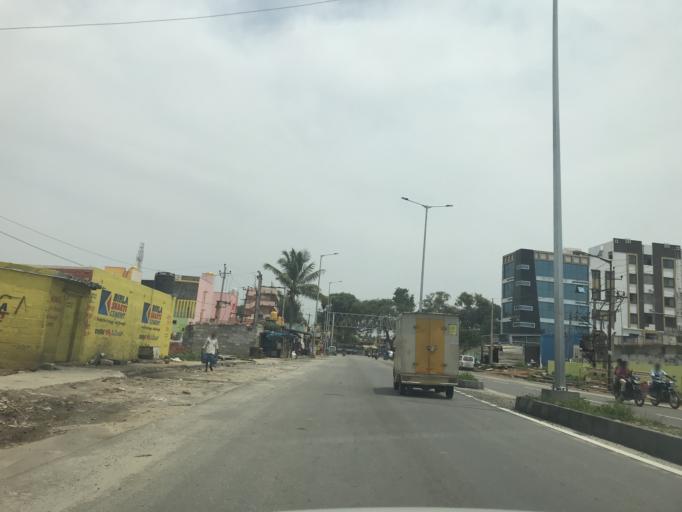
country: IN
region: Karnataka
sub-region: Bangalore Urban
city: Yelahanka
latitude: 13.0946
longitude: 77.6544
